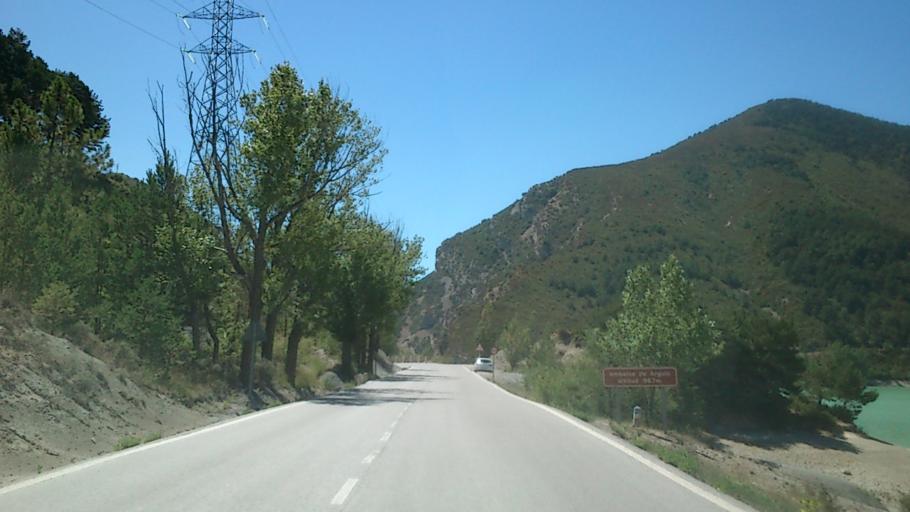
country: ES
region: Aragon
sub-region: Provincia de Huesca
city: Arguis
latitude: 42.3084
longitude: -0.4287
